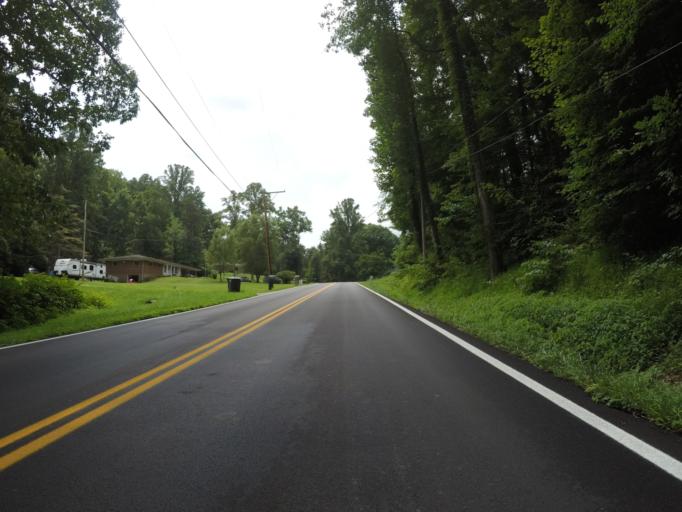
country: US
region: Kentucky
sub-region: Boyd County
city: Catlettsburg
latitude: 38.4309
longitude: -82.6294
